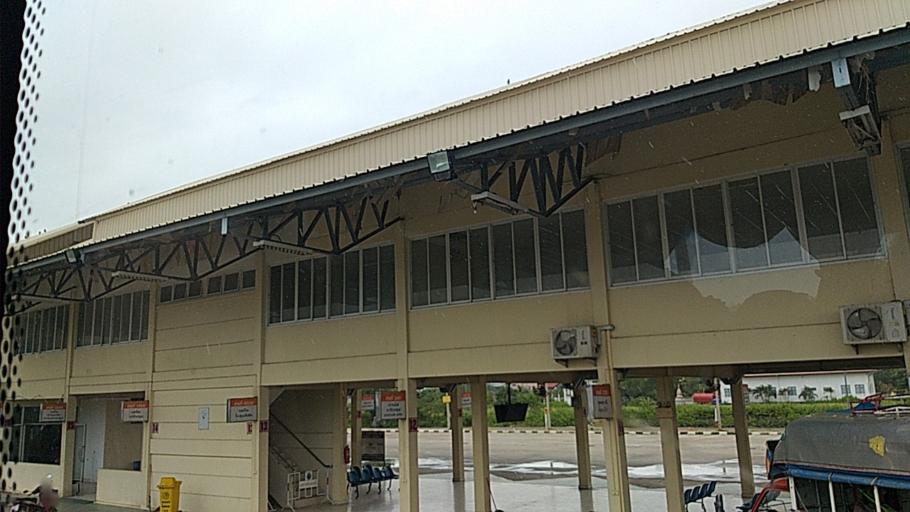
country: TH
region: Maha Sarakham
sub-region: Amphoe Borabue
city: Borabue
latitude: 16.0372
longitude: 103.1263
